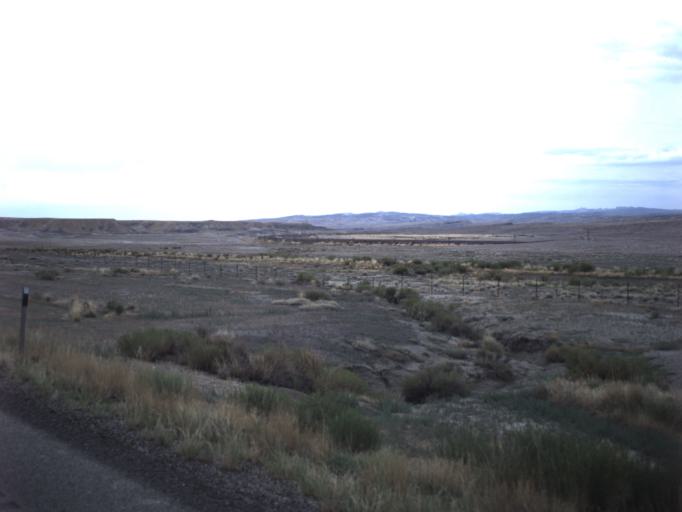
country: US
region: Utah
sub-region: Carbon County
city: East Carbon City
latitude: 39.3554
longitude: -110.3842
